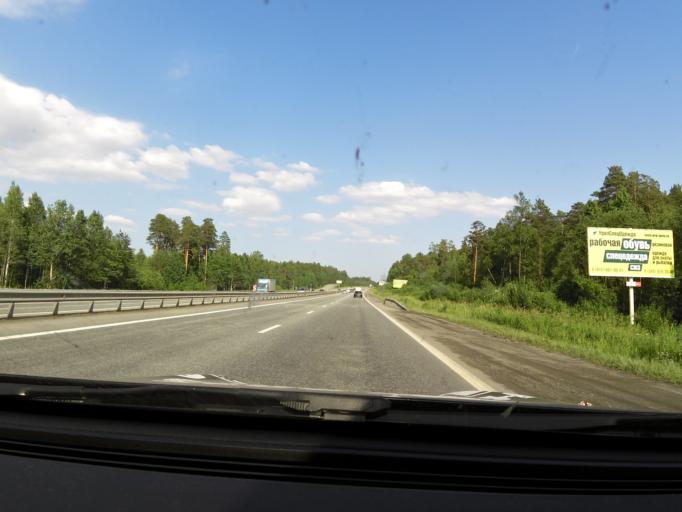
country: RU
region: Sverdlovsk
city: Severka
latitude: 56.8319
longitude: 60.3646
